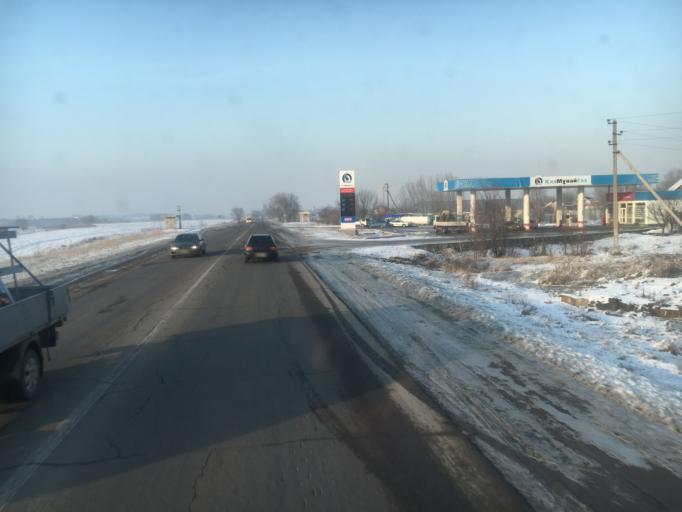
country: KZ
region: Almaty Oblysy
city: Burunday
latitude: 43.2894
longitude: 76.6734
